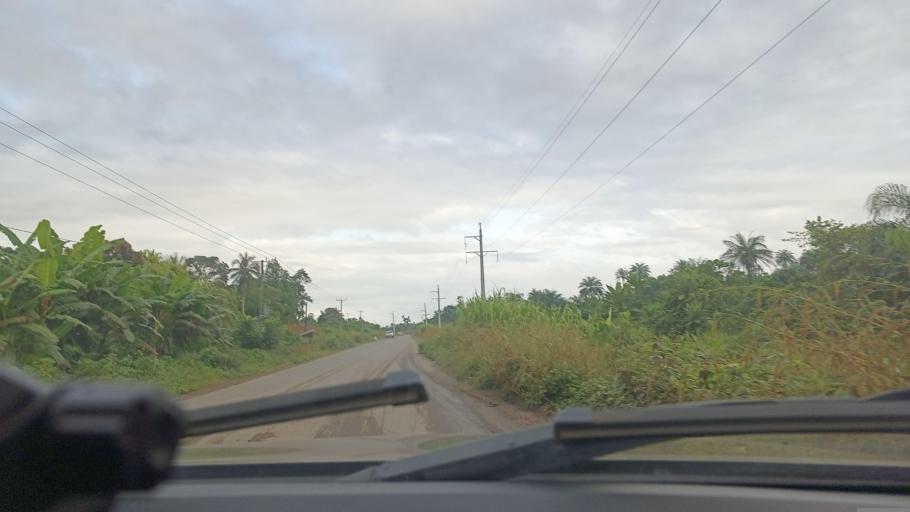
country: LR
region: Montserrado
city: Monrovia
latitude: 6.5636
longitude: -10.8726
